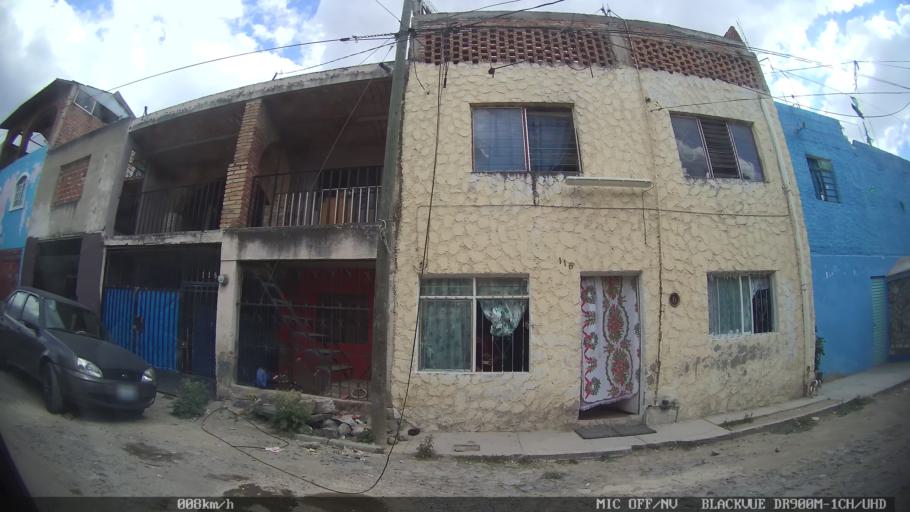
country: MX
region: Jalisco
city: Tlaquepaque
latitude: 20.6825
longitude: -103.2612
